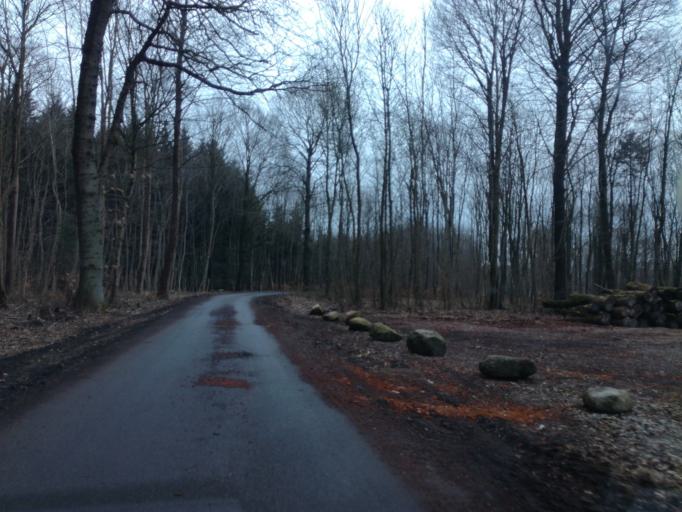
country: DK
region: South Denmark
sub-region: Vejle Kommune
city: Brejning
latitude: 55.6189
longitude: 9.7069
